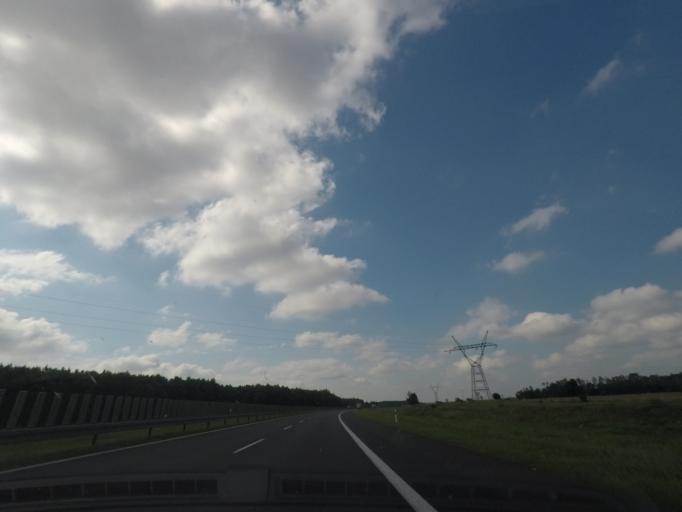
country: PL
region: Kujawsko-Pomorskie
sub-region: Powiat swiecki
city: Warlubie
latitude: 53.5499
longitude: 18.6132
